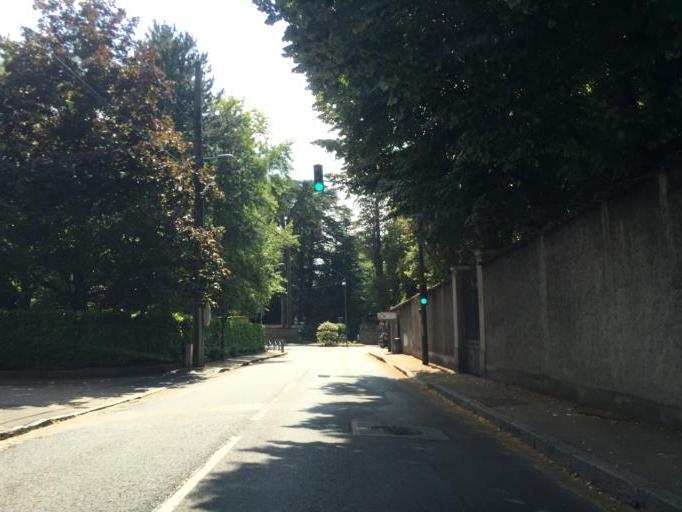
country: FR
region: Rhone-Alpes
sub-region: Departement du Rhone
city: Ecully
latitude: 45.7707
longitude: 4.7753
